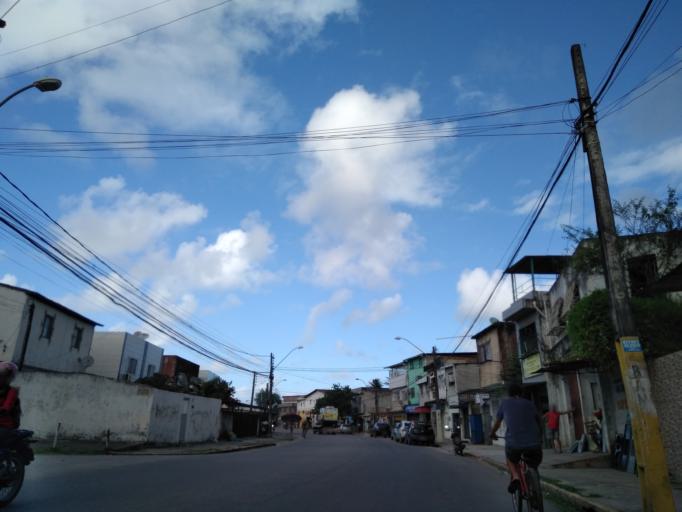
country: BR
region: Pernambuco
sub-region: Recife
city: Recife
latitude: -8.0740
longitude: -34.9230
